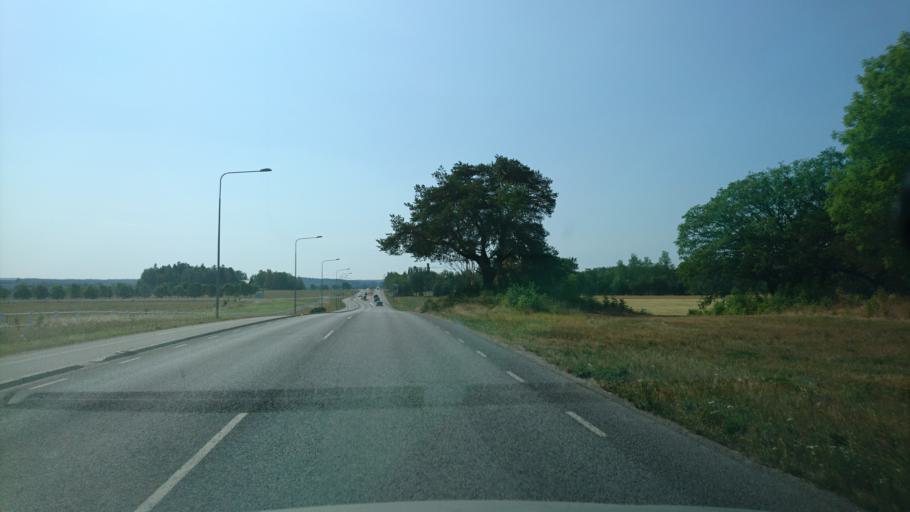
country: SE
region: Uppsala
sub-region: Uppsala Kommun
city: Uppsala
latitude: 59.8210
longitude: 17.6467
